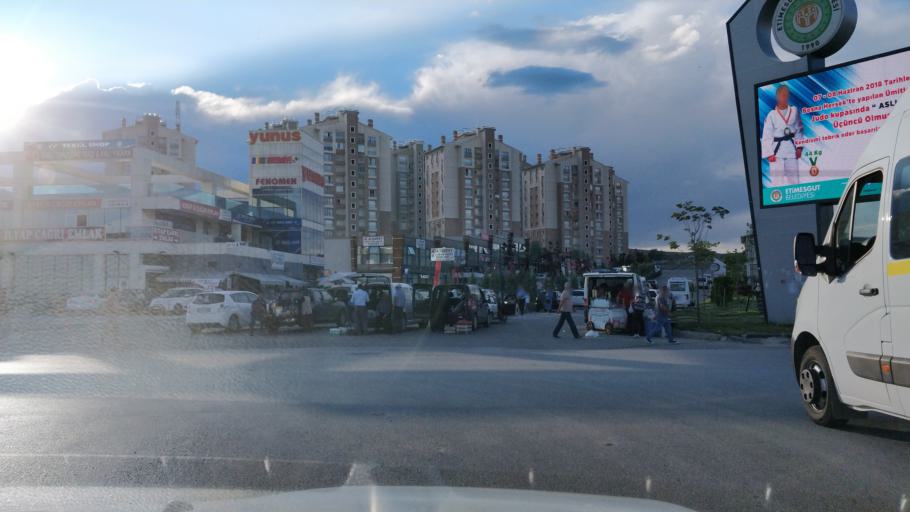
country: TR
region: Ankara
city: Etimesgut
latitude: 39.8430
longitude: 32.5469
